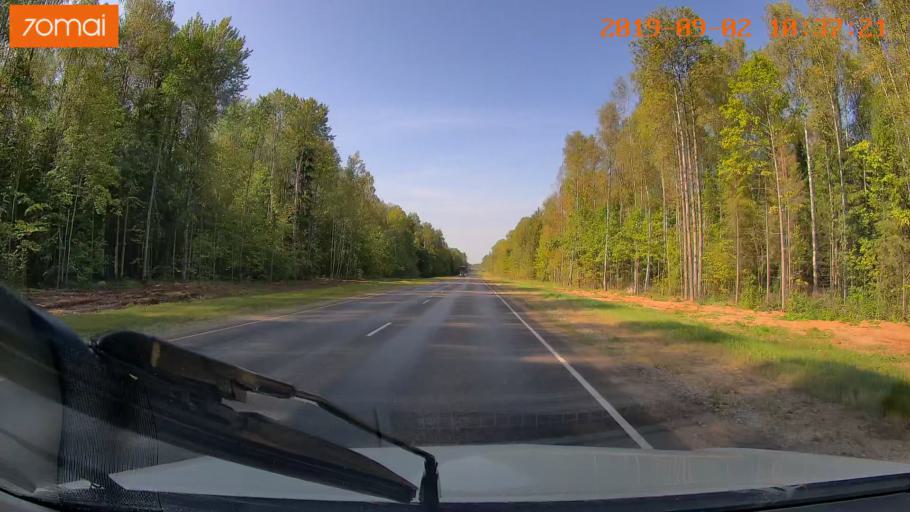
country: RU
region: Kaluga
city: Spas-Demensk
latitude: 54.2620
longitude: 33.7917
